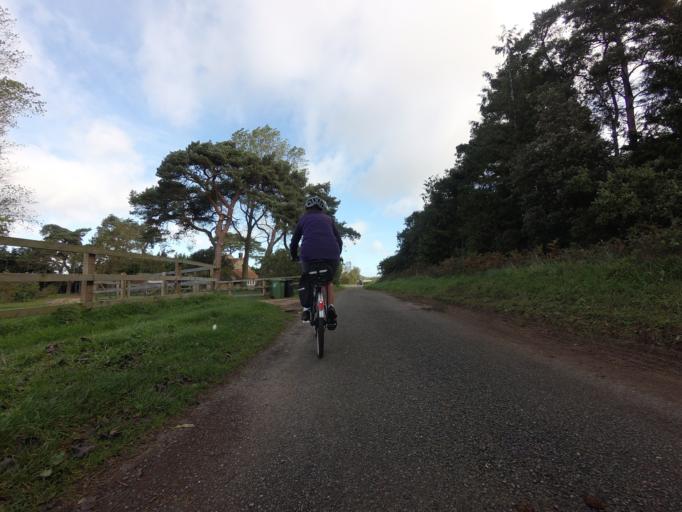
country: GB
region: England
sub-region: Norfolk
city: Dersingham
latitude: 52.8743
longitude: 0.6753
